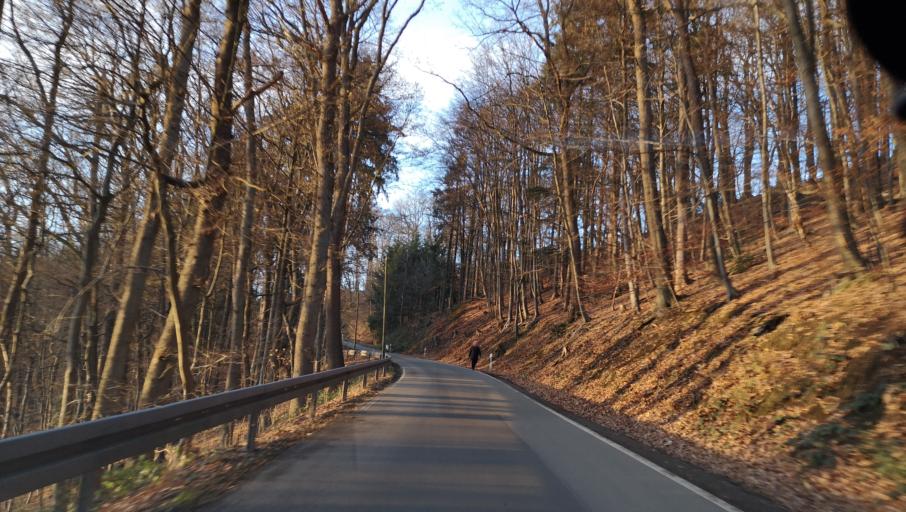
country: DE
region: North Rhine-Westphalia
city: Huckeswagen
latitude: 51.1573
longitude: 7.3399
